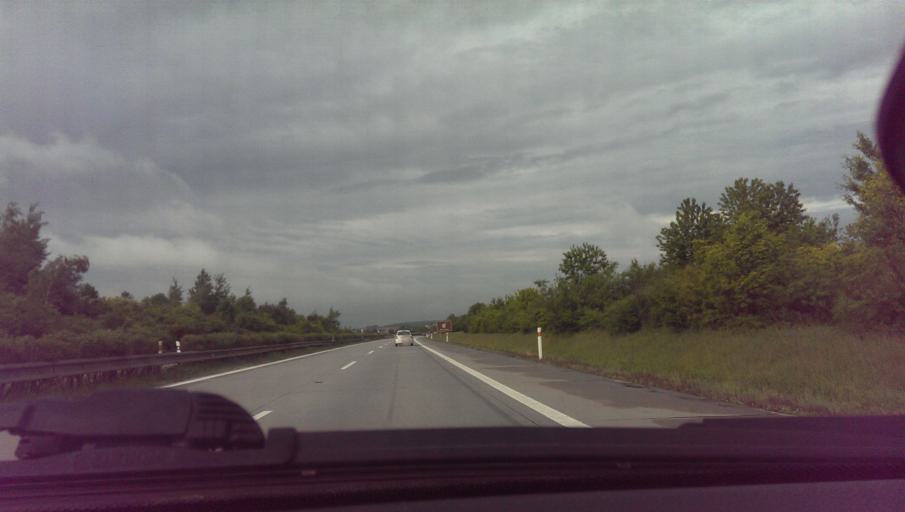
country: CZ
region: South Moravian
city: Ivanovice na Hane
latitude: 49.2841
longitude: 17.0805
